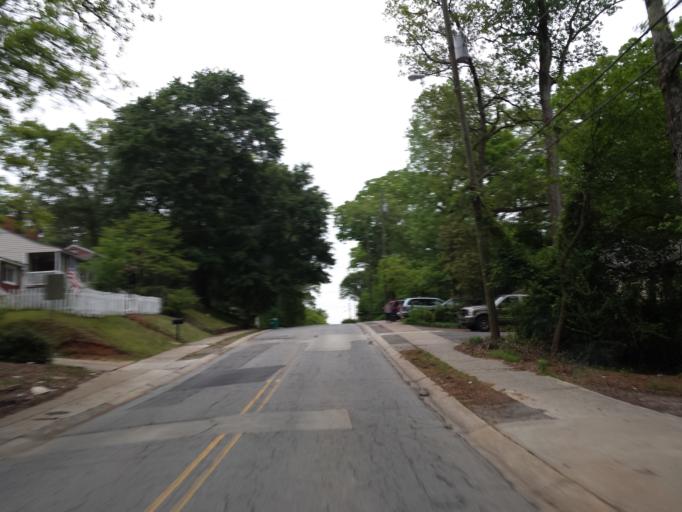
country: US
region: Georgia
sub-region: Cobb County
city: Marietta
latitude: 33.9406
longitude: -84.5513
